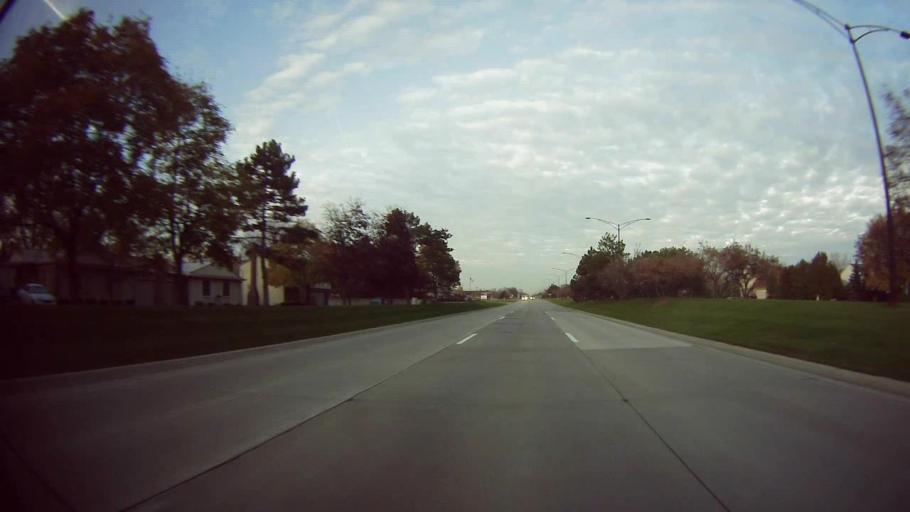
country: US
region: Michigan
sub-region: Oakland County
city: Clawson
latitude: 42.5636
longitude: -83.1026
